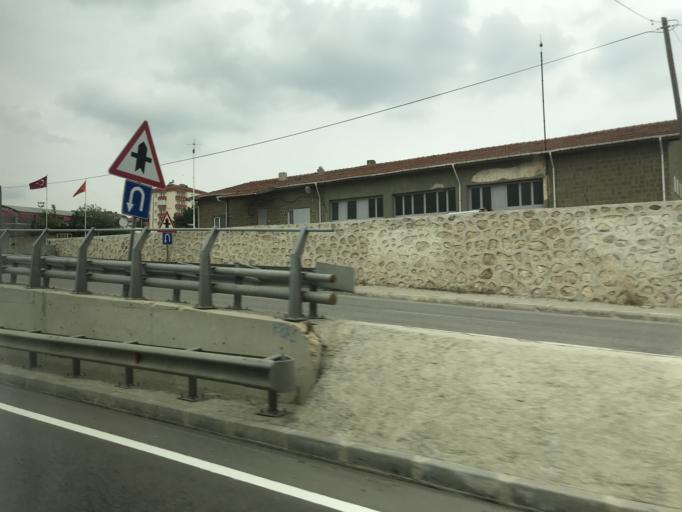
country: TR
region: Tekirdag
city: Malkara
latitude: 40.8853
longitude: 26.9160
